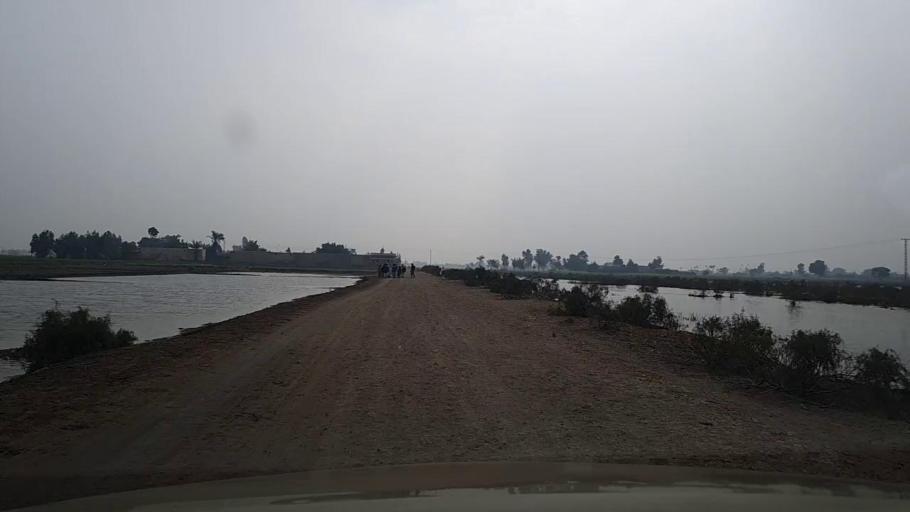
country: PK
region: Sindh
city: Sanghar
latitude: 26.1181
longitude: 68.9164
